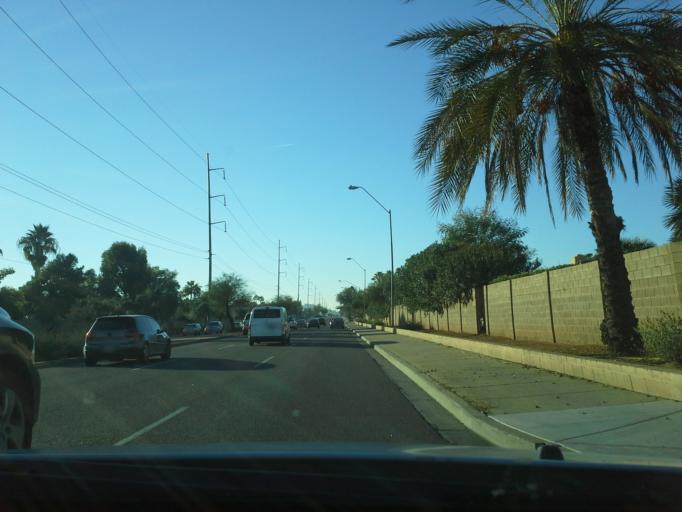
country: US
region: Arizona
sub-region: Maricopa County
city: Glendale
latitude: 33.6312
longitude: -112.0656
